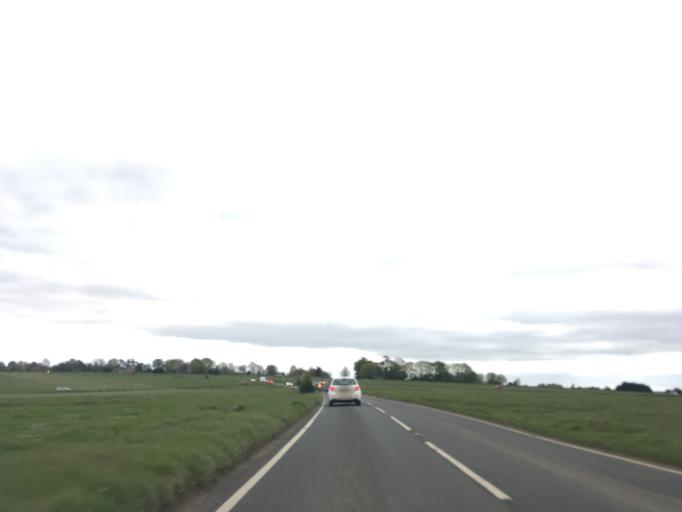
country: GB
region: England
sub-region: Gloucestershire
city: Nailsworth
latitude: 51.7119
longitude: -2.2092
